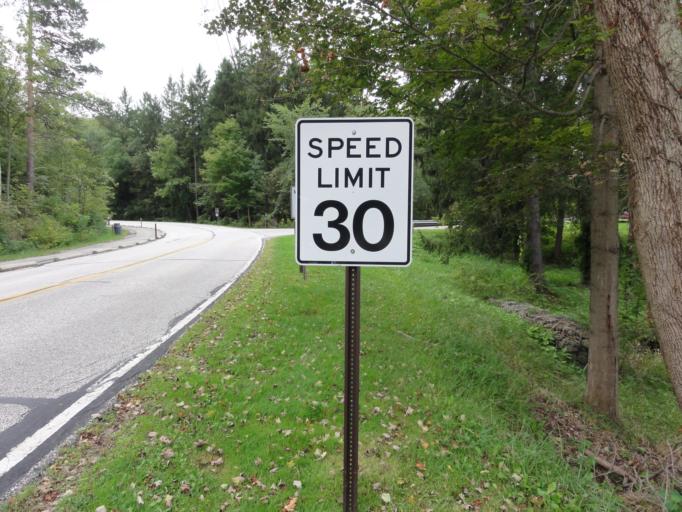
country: US
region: Ohio
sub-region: Summit County
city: Richfield
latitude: 41.2280
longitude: -81.7209
